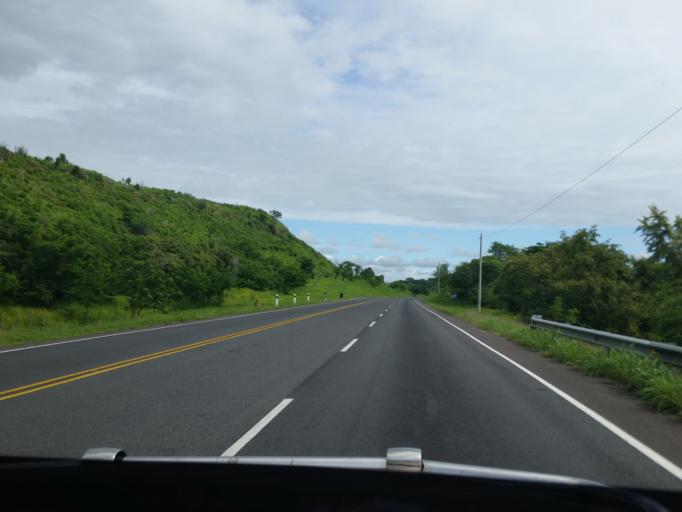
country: NI
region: Managua
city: Valle San Francisco
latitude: 12.5061
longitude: -86.0571
